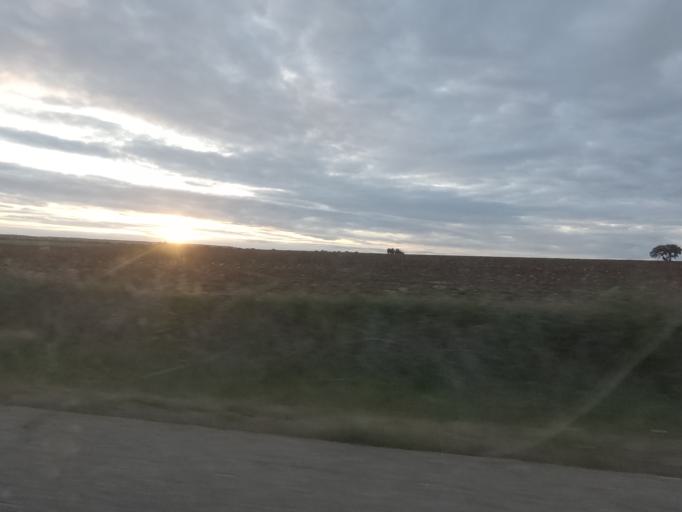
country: ES
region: Extremadura
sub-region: Provincia de Badajoz
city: Villar del Rey
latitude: 39.0509
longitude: -6.7997
